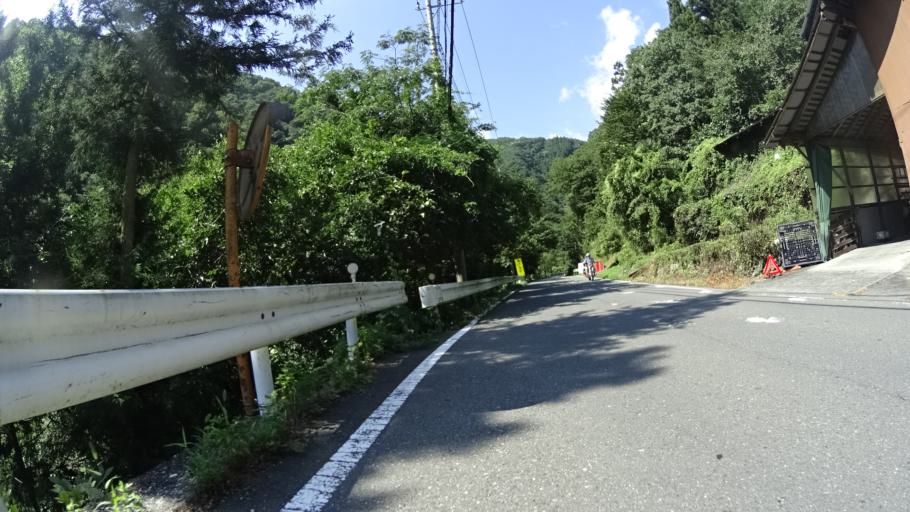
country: JP
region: Saitama
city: Chichibu
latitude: 36.0388
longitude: 138.9071
